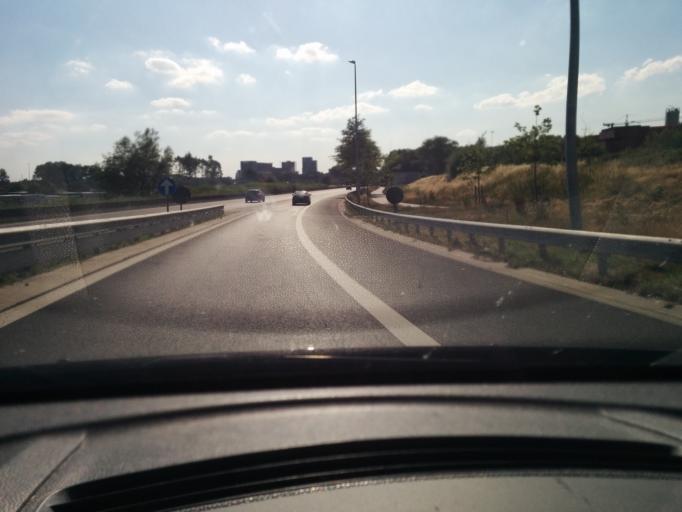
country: BE
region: Flanders
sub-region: Provincie Oost-Vlaanderen
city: Merelbeke
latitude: 51.0142
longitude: 3.7257
